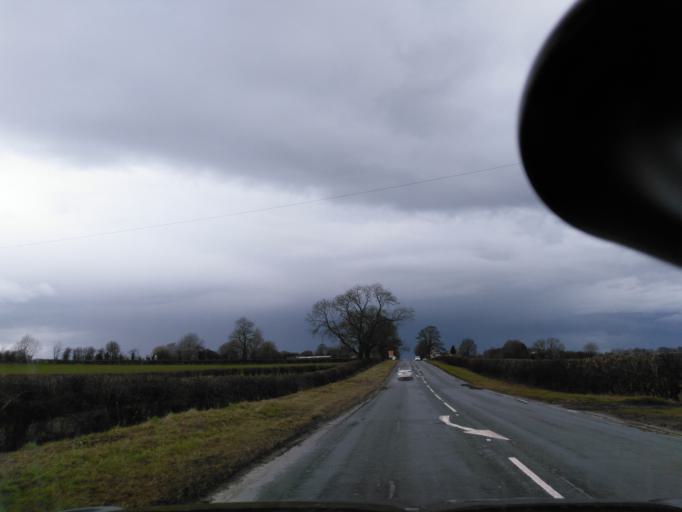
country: GB
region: England
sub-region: North Yorkshire
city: Ripon
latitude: 54.0873
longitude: -1.5301
